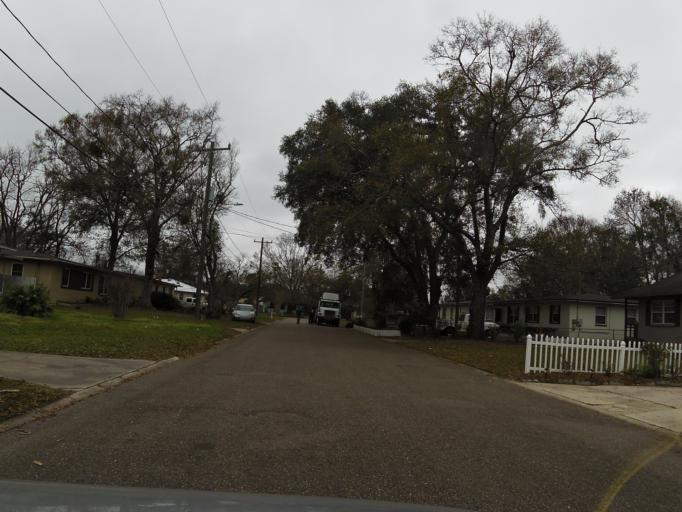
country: US
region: Florida
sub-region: Duval County
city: Jacksonville
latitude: 30.3714
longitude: -81.7146
